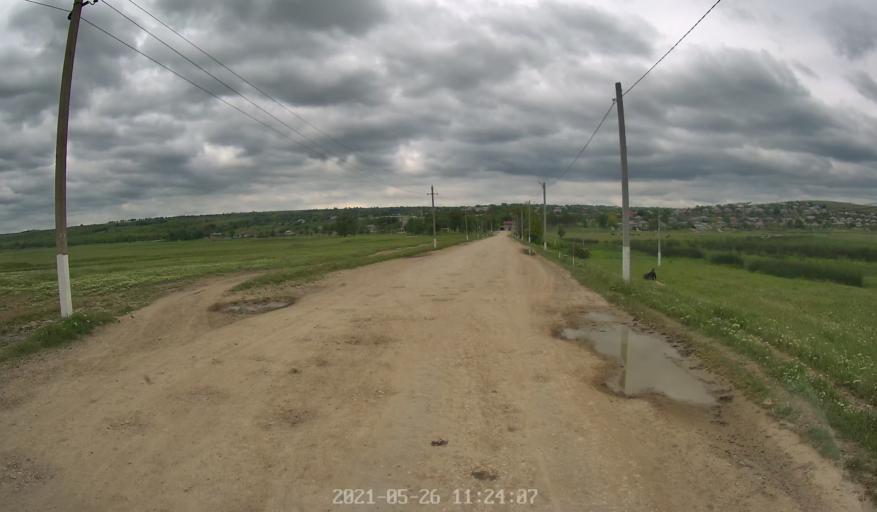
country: MD
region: Hincesti
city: Dancu
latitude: 46.8241
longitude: 28.3752
